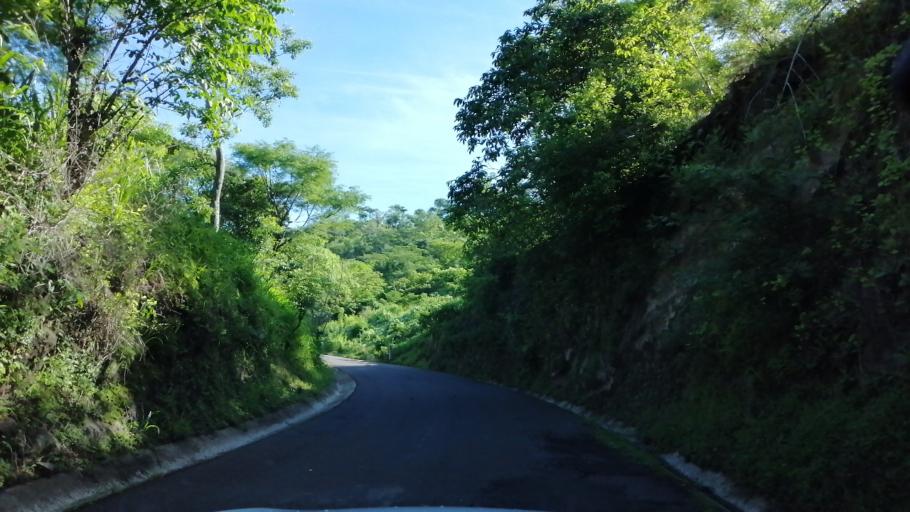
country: SV
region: Morazan
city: Corinto
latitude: 13.7969
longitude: -88.0073
